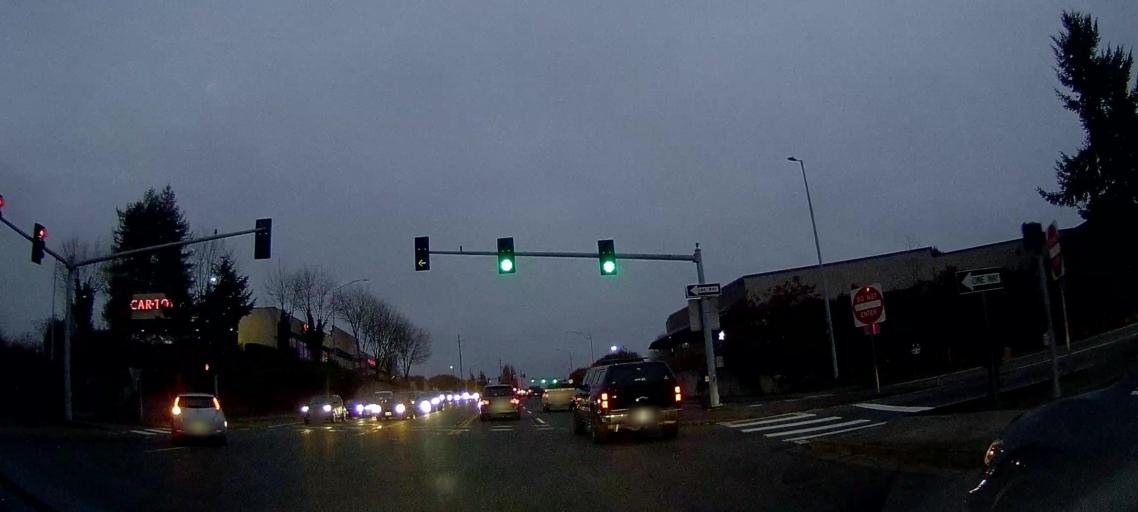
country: US
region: Washington
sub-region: Thurston County
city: Lacey
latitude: 47.0416
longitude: -122.8531
